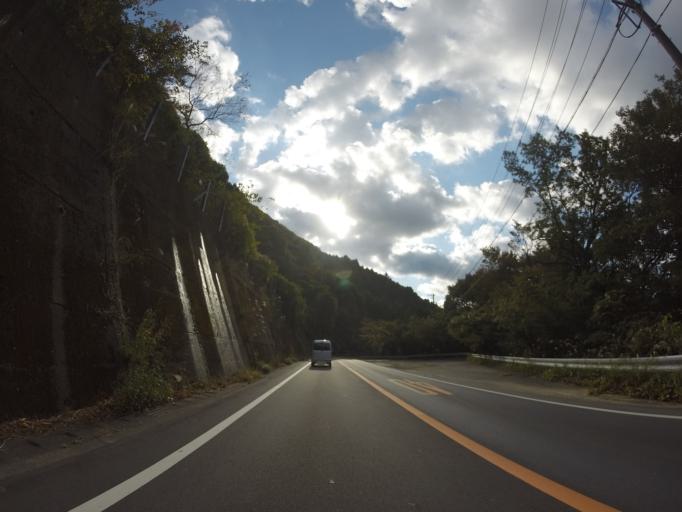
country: JP
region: Shizuoka
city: Kanaya
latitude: 34.8851
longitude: 138.1153
